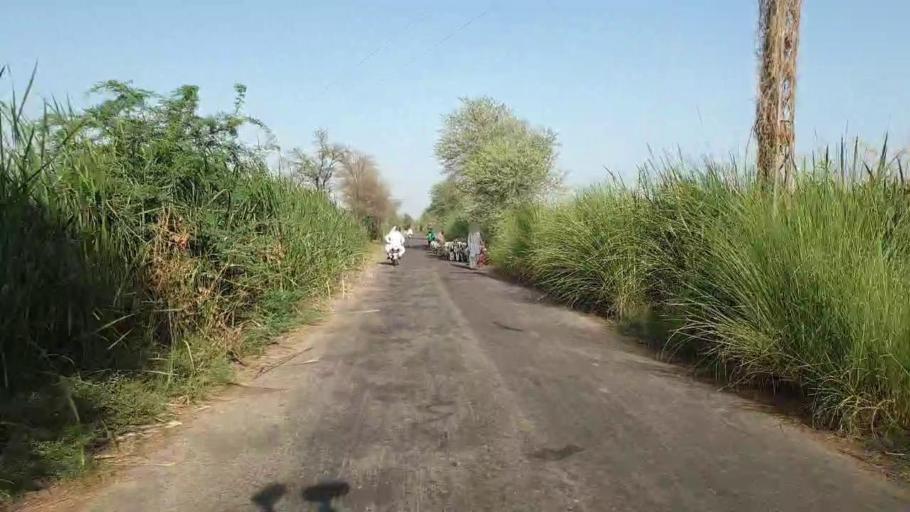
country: PK
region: Sindh
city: Nawabshah
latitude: 26.3755
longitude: 68.4645
